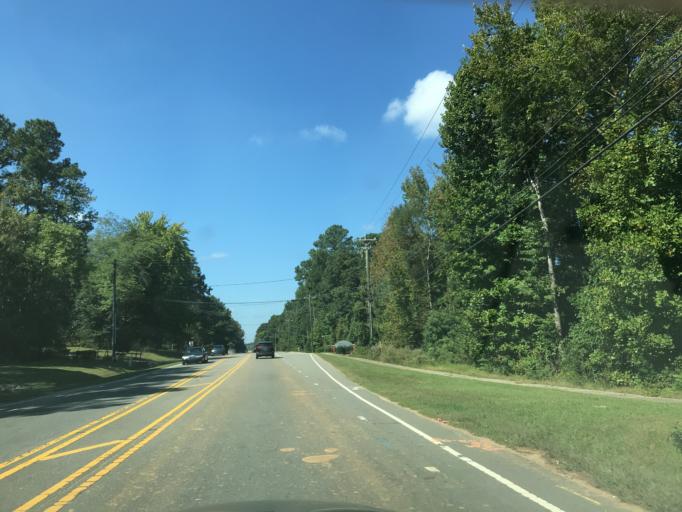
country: US
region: North Carolina
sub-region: Durham County
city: Durham
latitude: 35.9063
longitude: -78.9197
